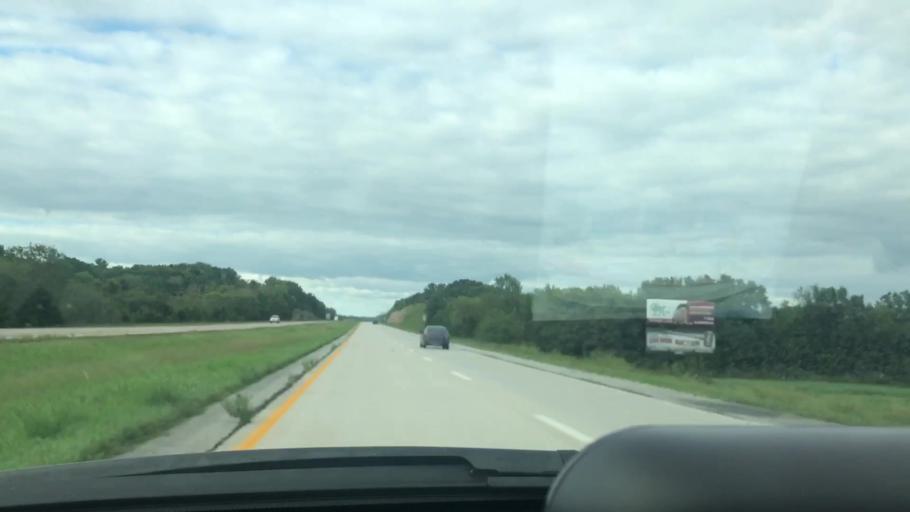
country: US
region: Missouri
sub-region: Benton County
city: Warsaw
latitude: 38.2699
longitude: -93.3667
